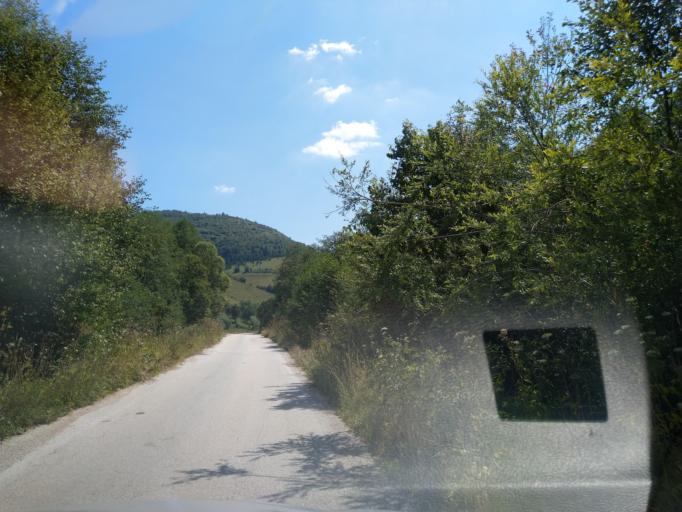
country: RS
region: Central Serbia
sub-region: Zlatiborski Okrug
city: Nova Varos
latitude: 43.4806
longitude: 19.9783
